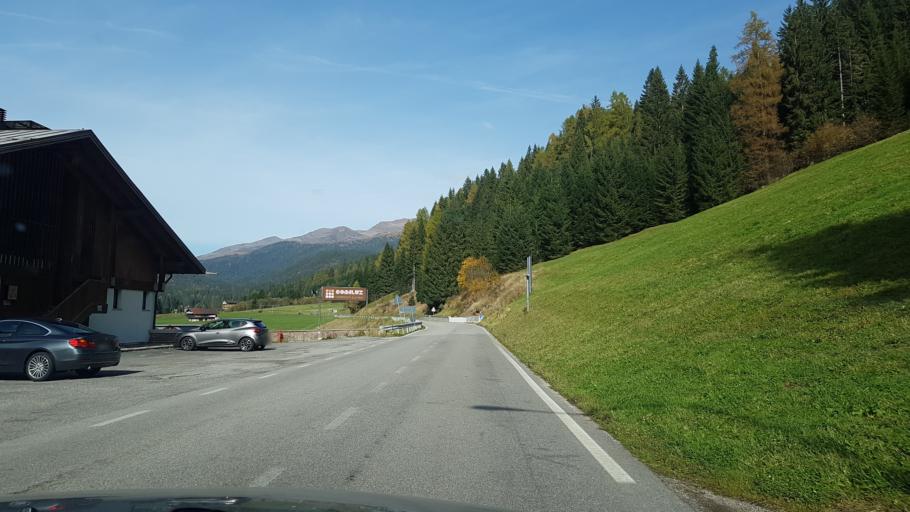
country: IT
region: Veneto
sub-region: Provincia di Belluno
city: Candide
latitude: 46.6099
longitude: 12.4807
